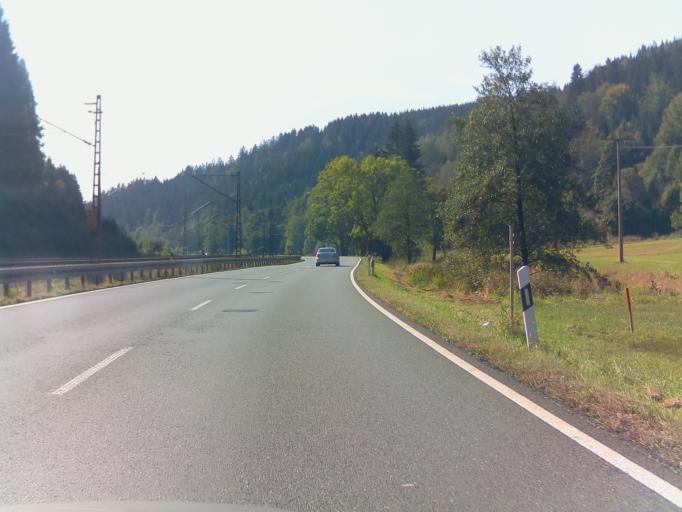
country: DE
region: Bavaria
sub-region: Upper Franconia
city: Pressig
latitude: 50.3777
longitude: 11.3383
